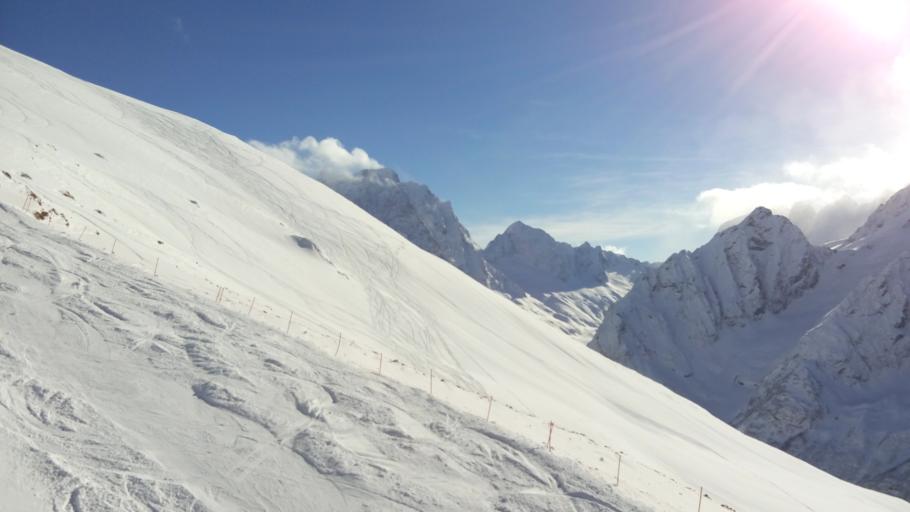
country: RU
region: Karachayevo-Cherkesiya
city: Teberda
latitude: 43.2912
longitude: 41.6645
